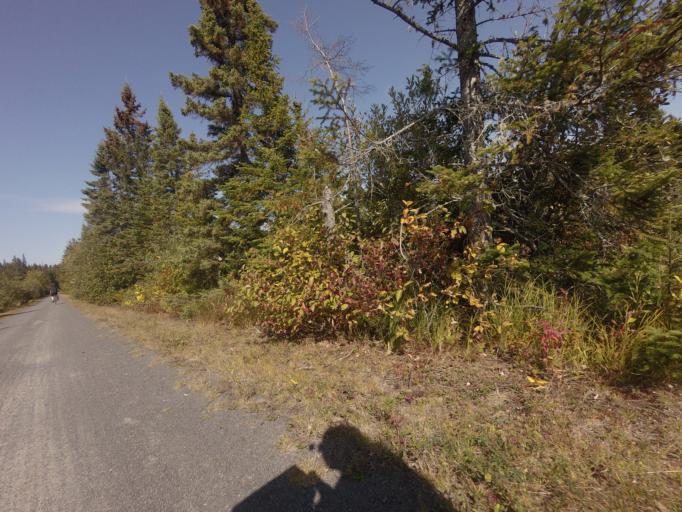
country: CA
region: Quebec
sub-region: Laurentides
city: Sainte-Agathe-des-Monts
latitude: 46.0888
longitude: -74.3431
